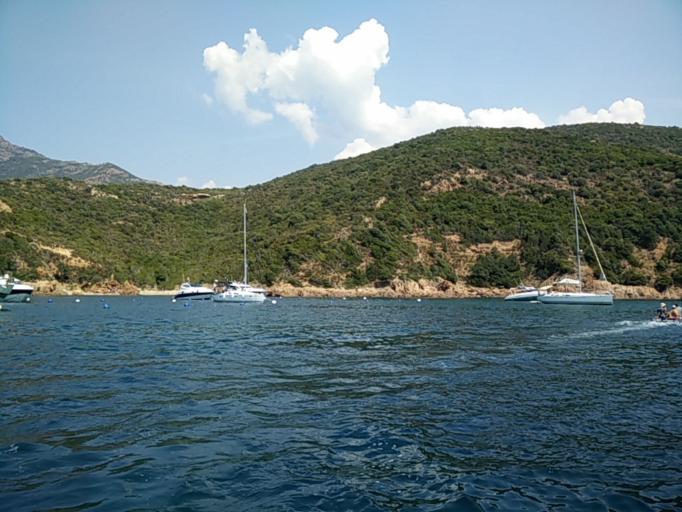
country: FR
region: Corsica
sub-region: Departement de la Corse-du-Sud
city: Cargese
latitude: 42.3475
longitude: 8.6146
